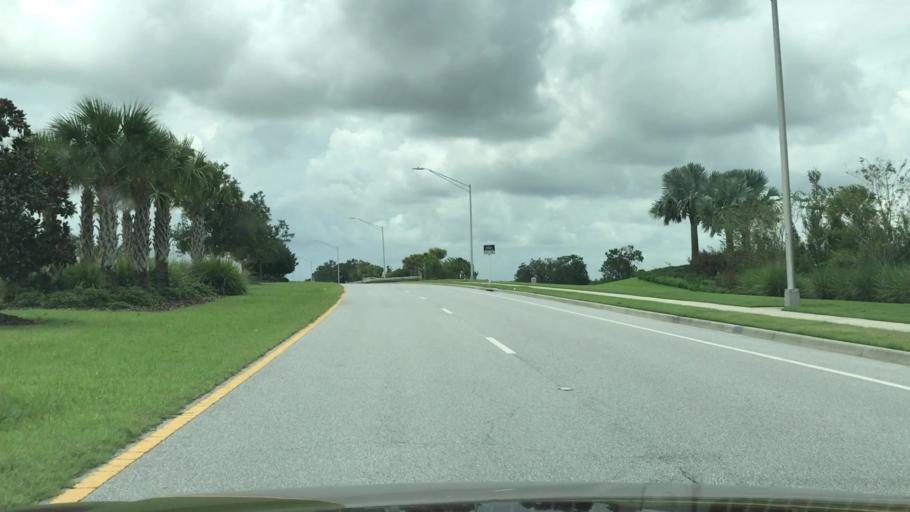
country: US
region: Florida
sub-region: Sarasota County
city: The Meadows
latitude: 27.4503
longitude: -82.4179
